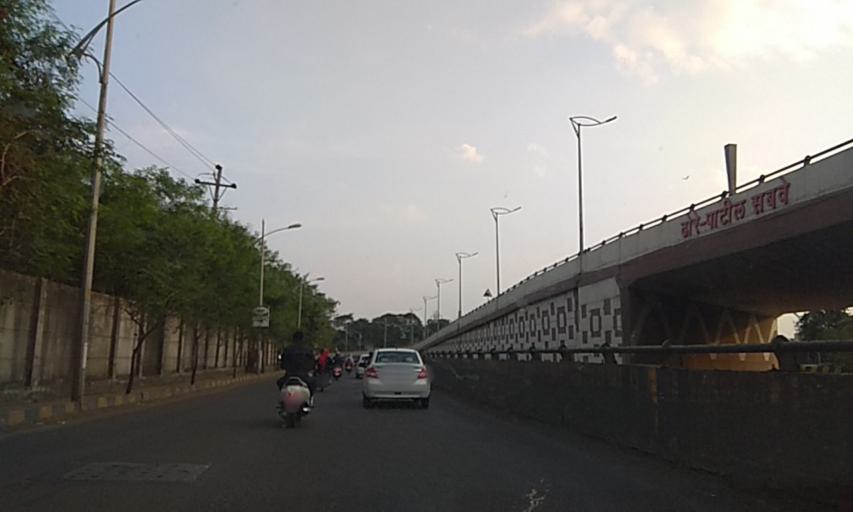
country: IN
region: Maharashtra
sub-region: Pune Division
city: Khadki
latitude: 18.5709
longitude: 73.8086
